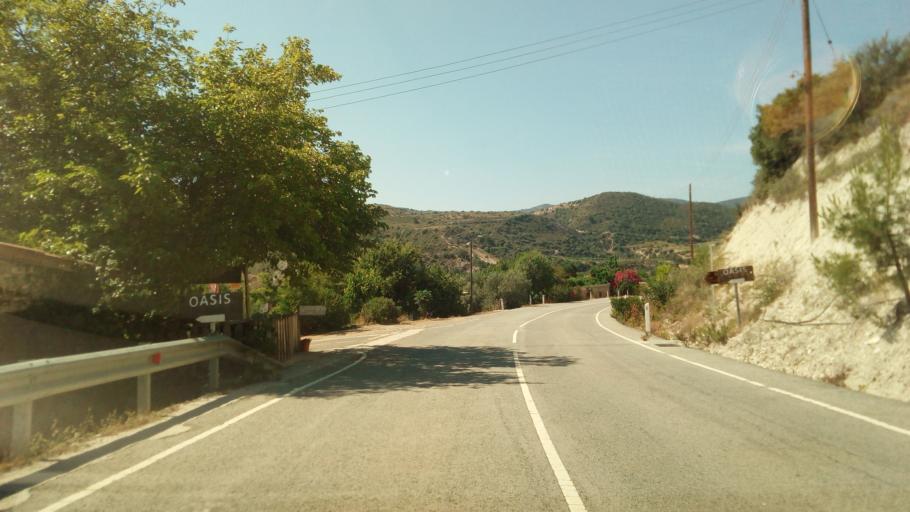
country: CY
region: Limassol
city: Pachna
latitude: 34.8077
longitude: 32.7125
